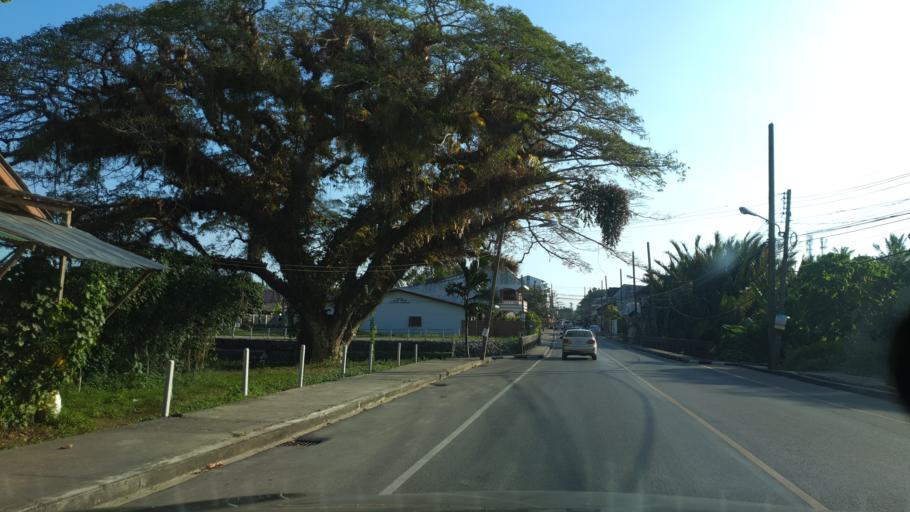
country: TH
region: Krabi
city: Krabi
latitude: 8.1041
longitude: 98.9116
